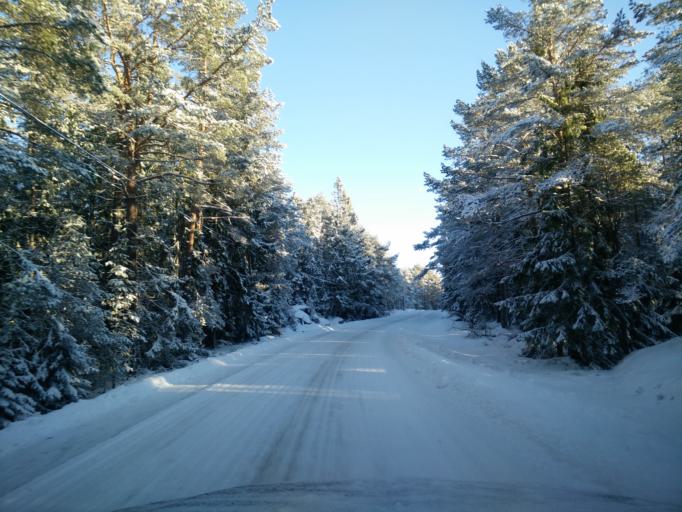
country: SE
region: Vaesternorrland
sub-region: Sundsvalls Kommun
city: Njurundabommen
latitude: 62.2331
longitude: 17.6363
